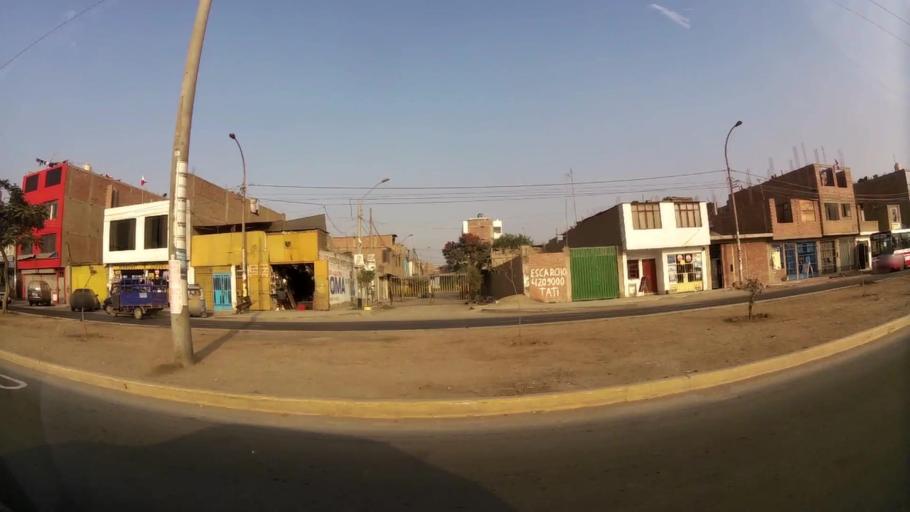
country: PE
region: Lima
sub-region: Lima
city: Independencia
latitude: -11.9765
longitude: -77.0918
